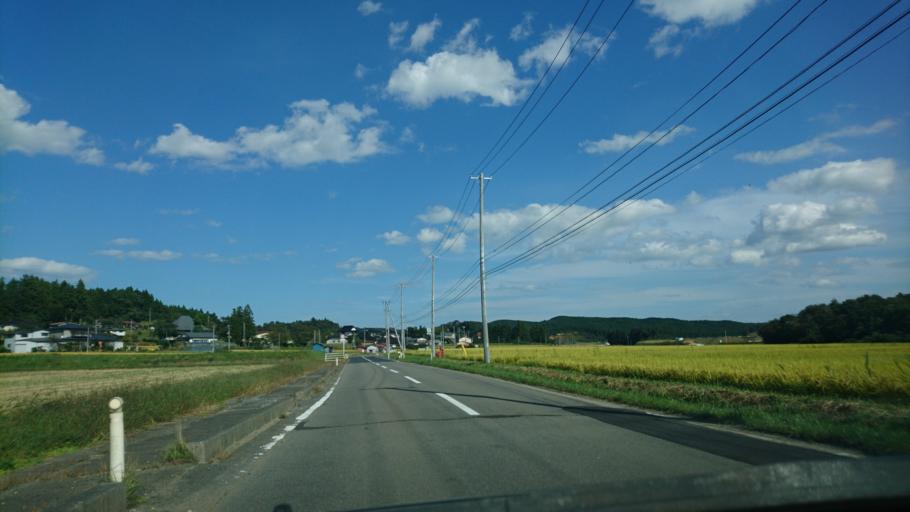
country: JP
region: Iwate
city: Ichinoseki
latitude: 38.8415
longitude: 141.0229
